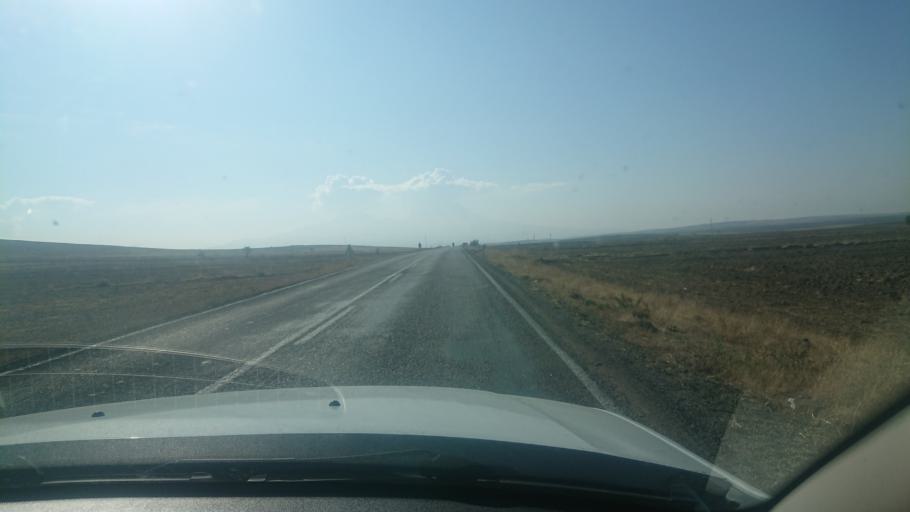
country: TR
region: Aksaray
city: Guzelyurt
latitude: 38.3078
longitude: 34.3252
